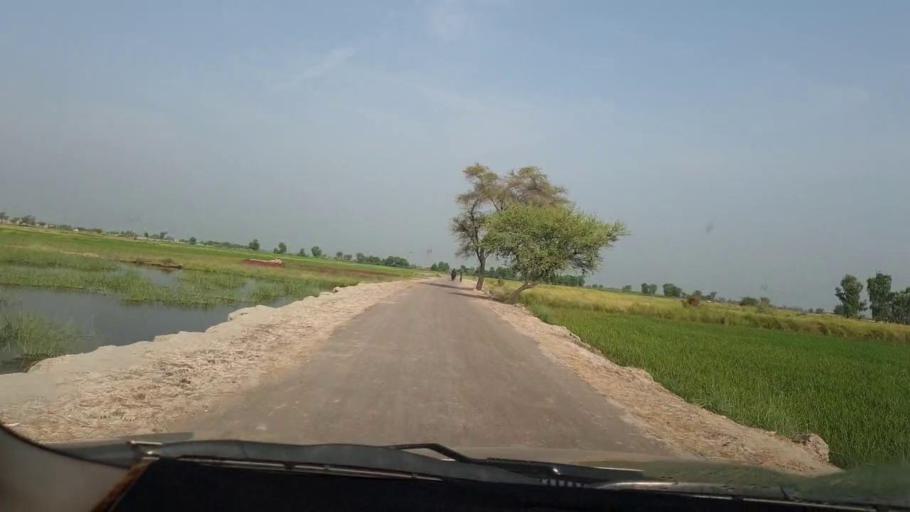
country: PK
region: Sindh
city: Goth Garelo
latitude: 27.4682
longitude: 68.0803
